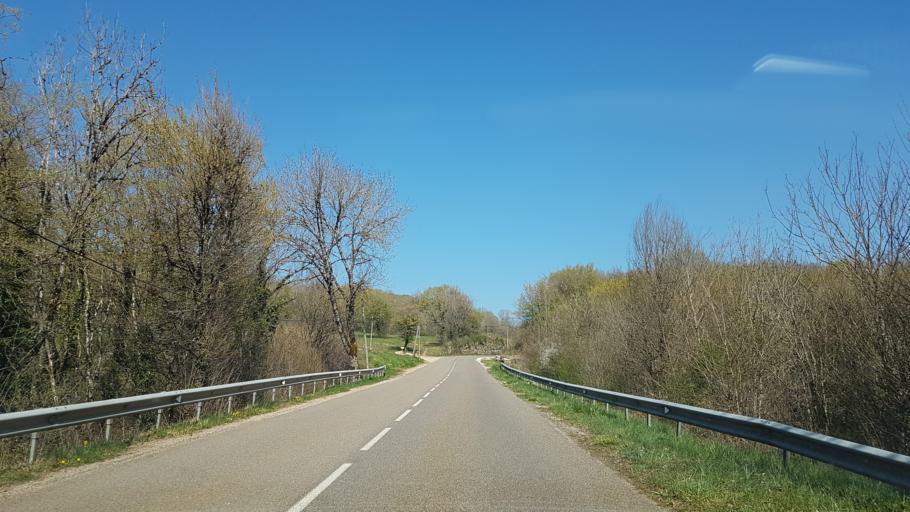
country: FR
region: Bourgogne
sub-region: Departement de Saone-et-Loire
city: Cuiseaux
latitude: 46.4564
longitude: 5.3926
